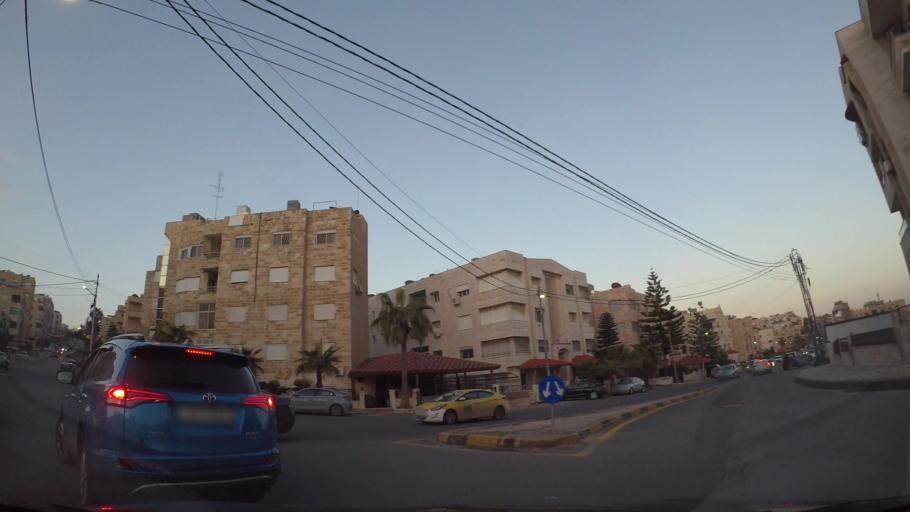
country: JO
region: Amman
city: Al Jubayhah
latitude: 31.9878
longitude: 35.8847
